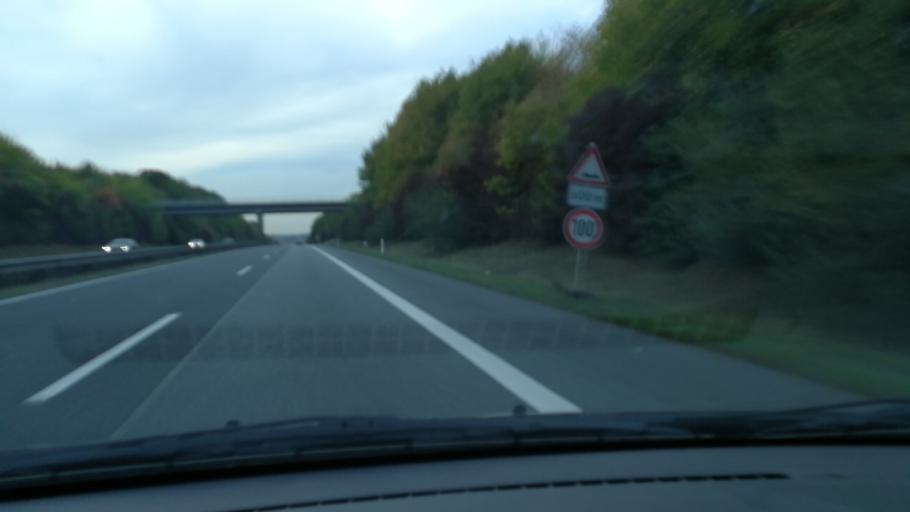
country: DE
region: Hesse
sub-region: Regierungsbezirk Darmstadt
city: Bad Vilbel
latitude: 50.1683
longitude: 8.7029
